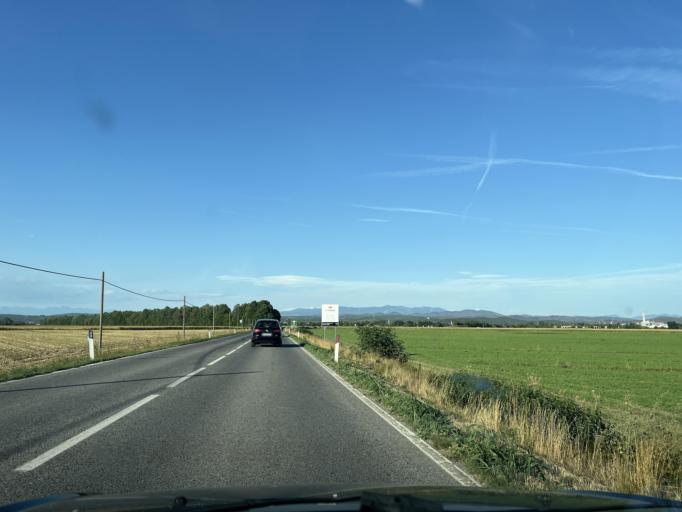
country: IT
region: Friuli Venezia Giulia
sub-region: Provincia di Gorizia
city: San Canzian d'Isonzo
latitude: 45.7895
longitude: 13.4799
